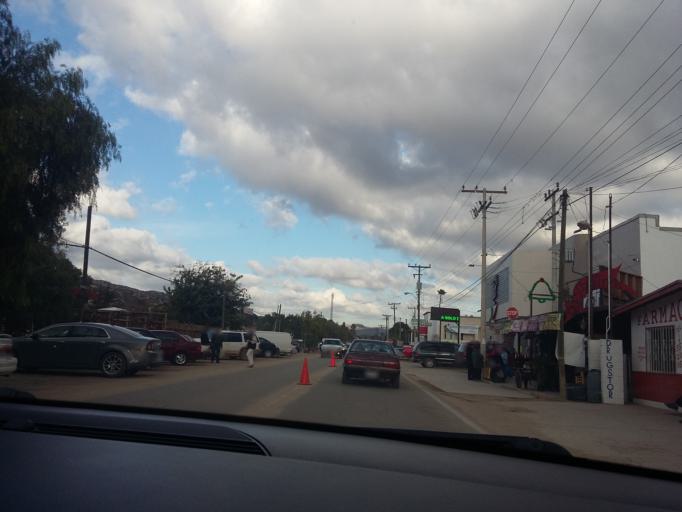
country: MX
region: Baja California
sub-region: Ensenada
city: Rancho Verde
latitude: 32.0948
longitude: -116.5741
